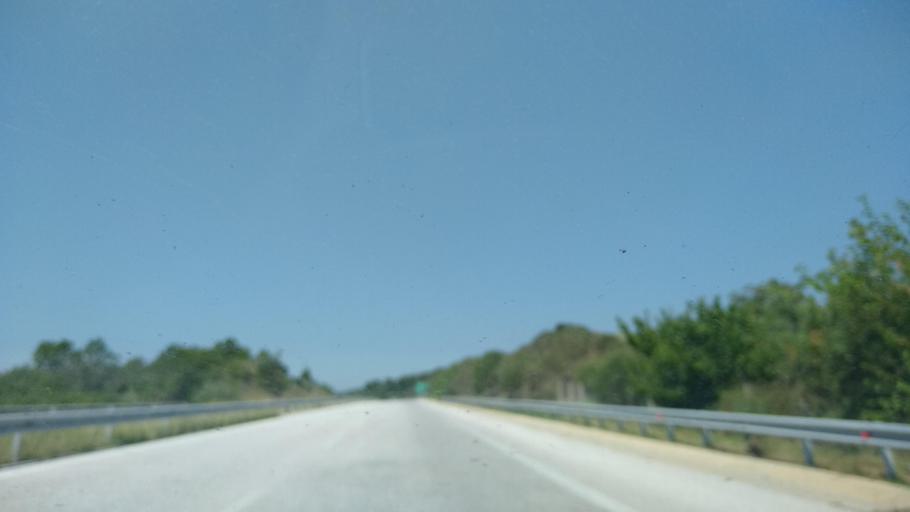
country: GR
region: Central Macedonia
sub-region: Nomos Thessalonikis
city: Gerakarou
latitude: 40.6936
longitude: 23.2838
